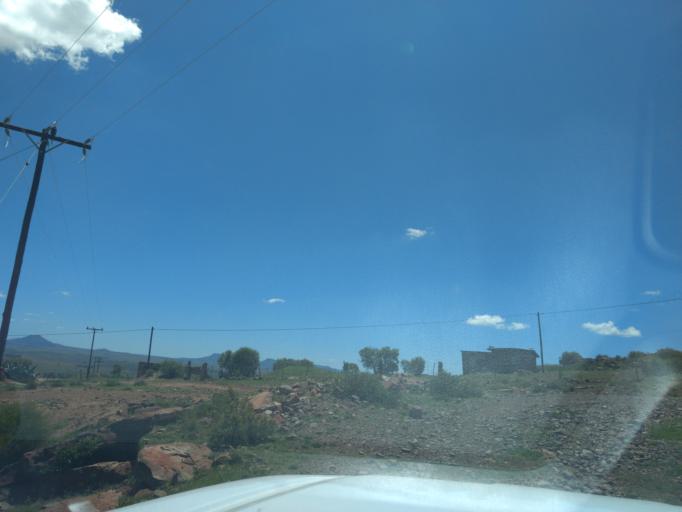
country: LS
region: Maseru
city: Maseru
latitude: -29.4565
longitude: 27.3754
